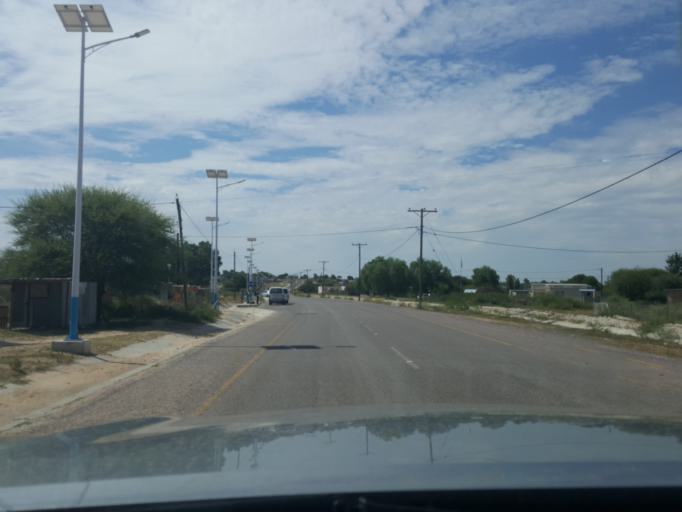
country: BW
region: Kweneng
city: Letlhakeng
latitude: -24.0951
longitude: 25.0299
